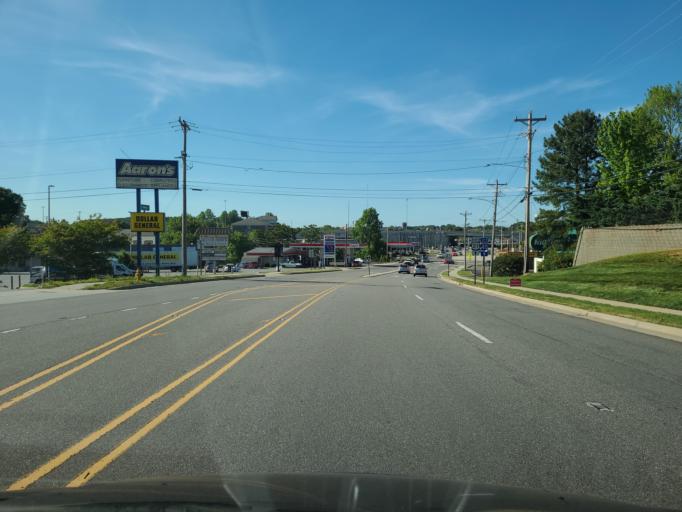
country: US
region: North Carolina
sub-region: Iredell County
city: Statesville
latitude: 35.8035
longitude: -80.8762
